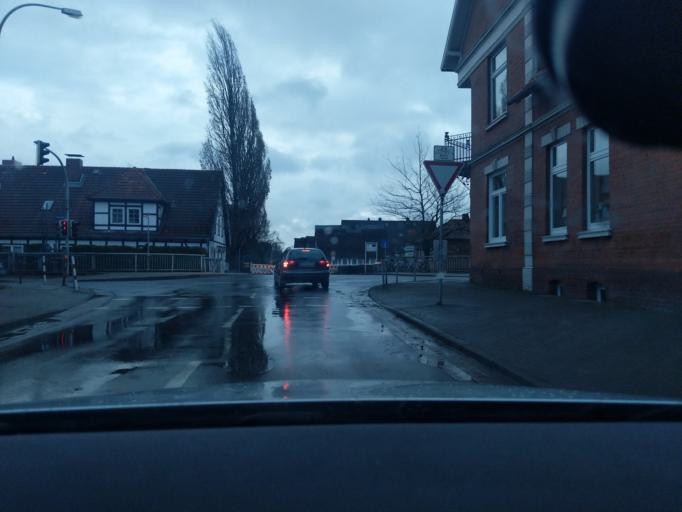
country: DE
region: Lower Saxony
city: Jork
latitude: 53.5185
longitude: 9.6706
